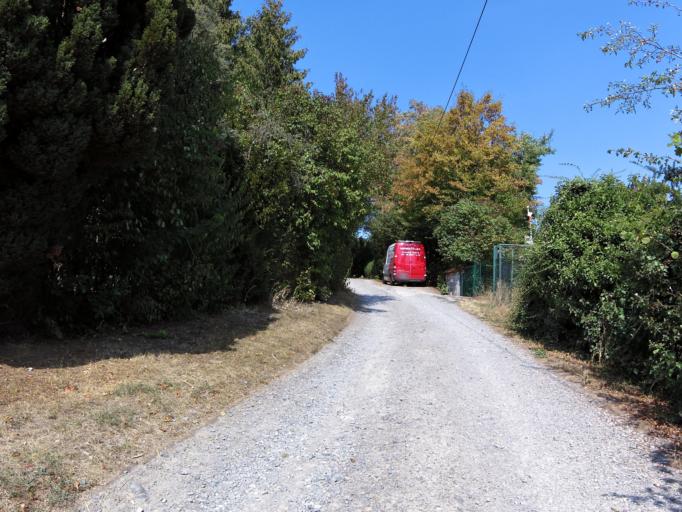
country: DE
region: Bavaria
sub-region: Regierungsbezirk Unterfranken
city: Zell am Main
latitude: 49.8231
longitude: 9.8626
